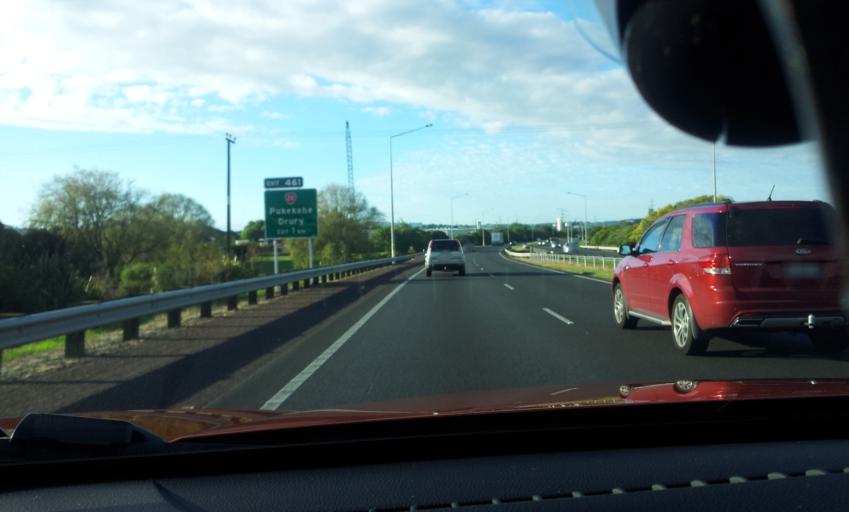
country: NZ
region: Auckland
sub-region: Auckland
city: Papakura
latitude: -37.0938
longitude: 174.9434
